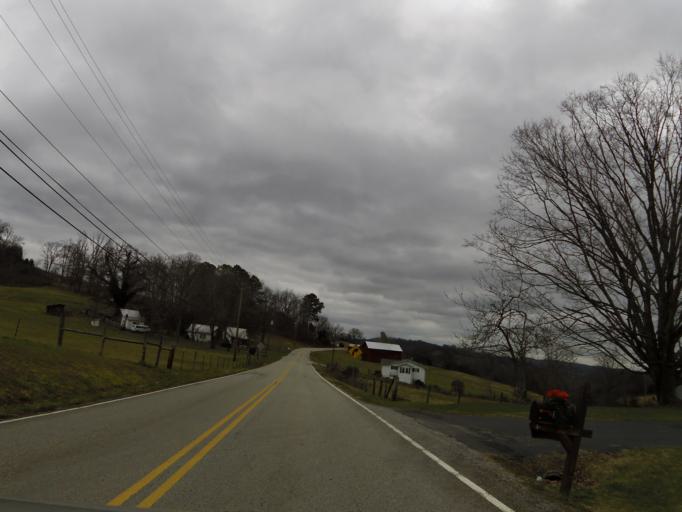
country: US
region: Tennessee
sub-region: Grainger County
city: Blaine
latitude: 36.1449
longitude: -83.6508
